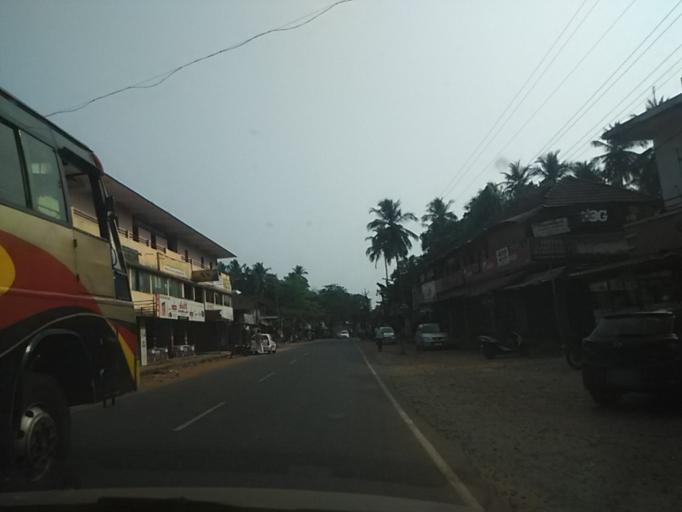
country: IN
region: Kerala
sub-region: Kozhikode
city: Naduvannur
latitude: 11.4847
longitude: 75.7751
